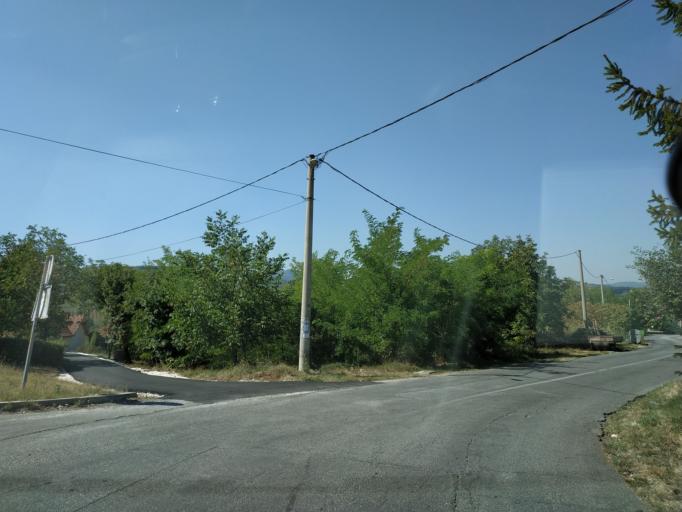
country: RS
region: Central Serbia
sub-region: Sumadijski Okrug
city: Topola
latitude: 44.2552
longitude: 20.6742
